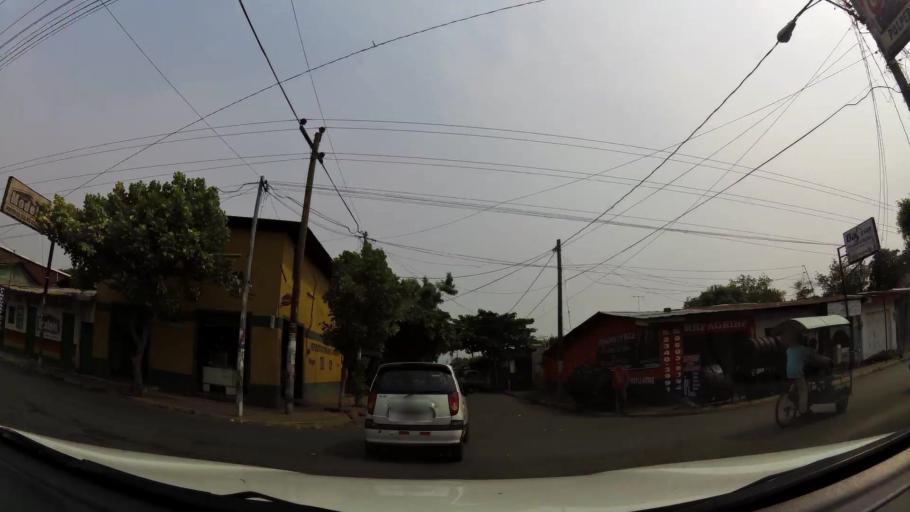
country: NI
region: Chinandega
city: Chinandega
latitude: 12.6256
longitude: -87.1274
